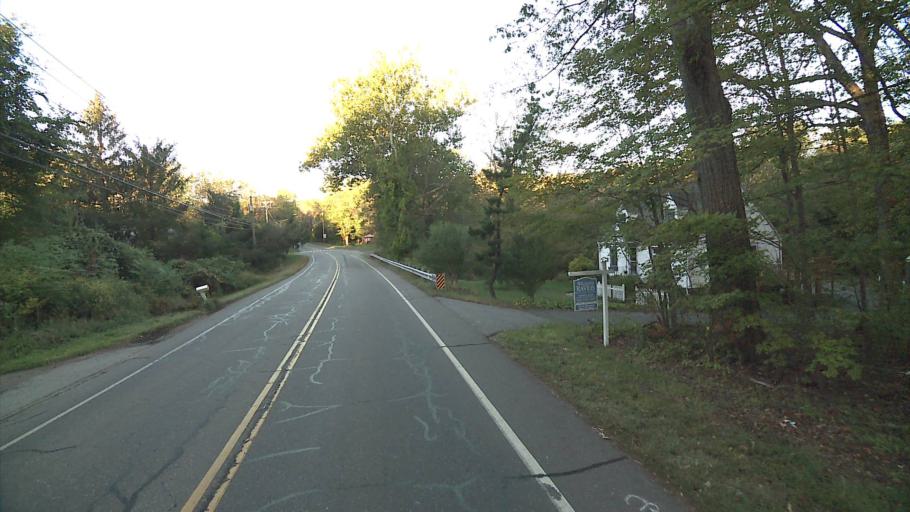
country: US
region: Connecticut
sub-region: Middlesex County
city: Durham
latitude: 41.4752
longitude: -72.7028
